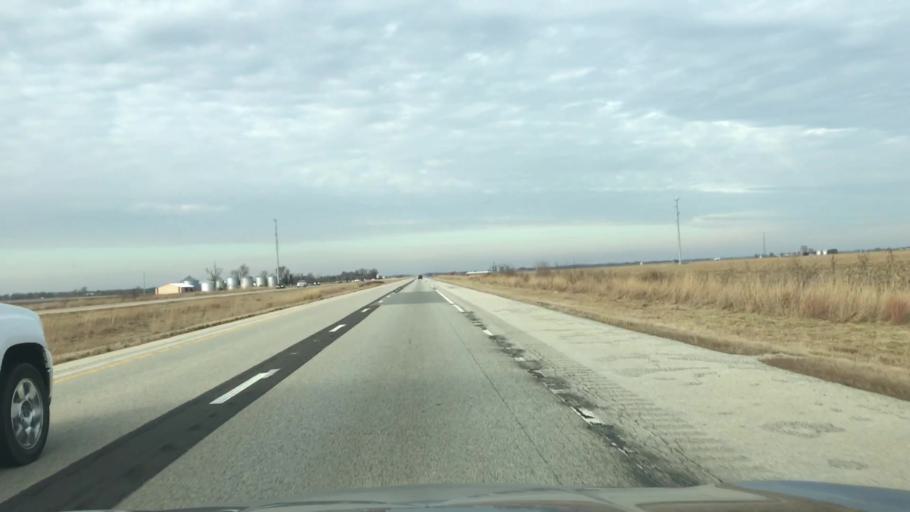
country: US
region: Illinois
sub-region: Sangamon County
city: Divernon
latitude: 39.5264
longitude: -89.6454
